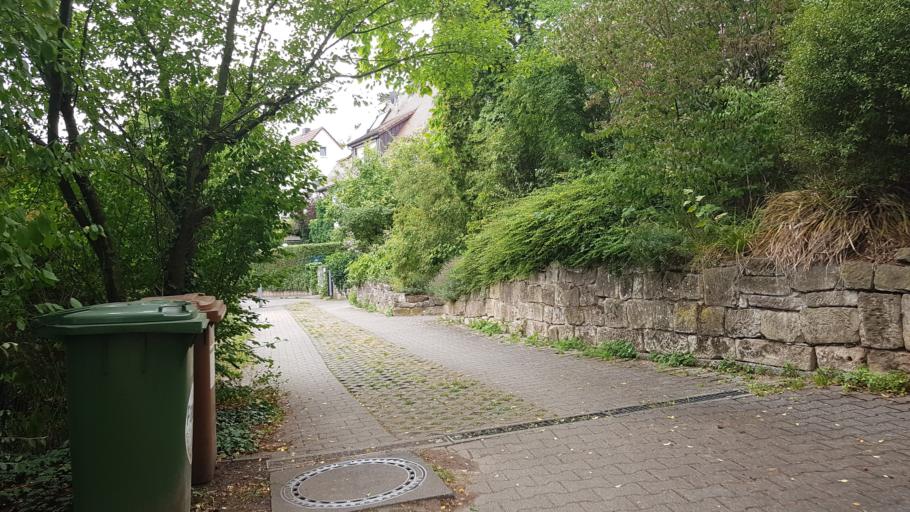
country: DE
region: Baden-Wuerttemberg
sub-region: Regierungsbezirk Stuttgart
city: Stuttgart-Ost
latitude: 48.7835
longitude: 9.2001
